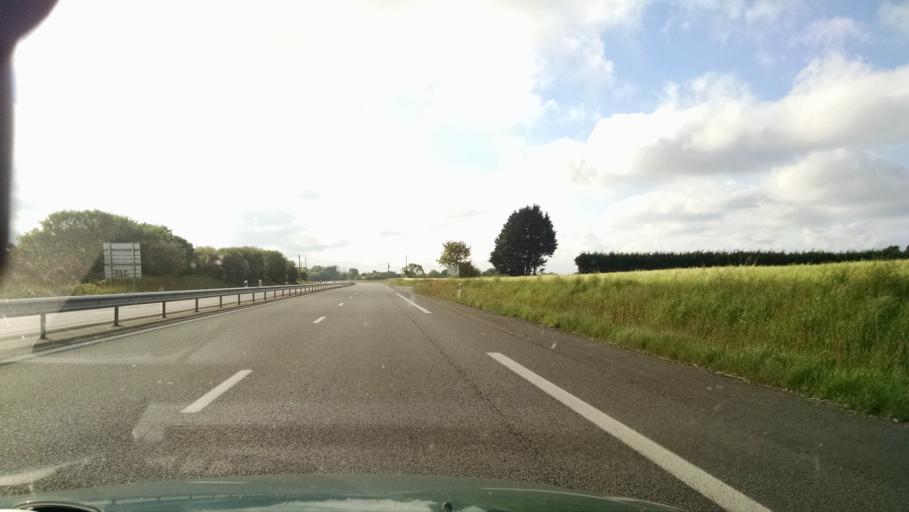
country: FR
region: Brittany
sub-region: Departement du Finistere
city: Henvic
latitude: 48.6256
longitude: -3.9087
